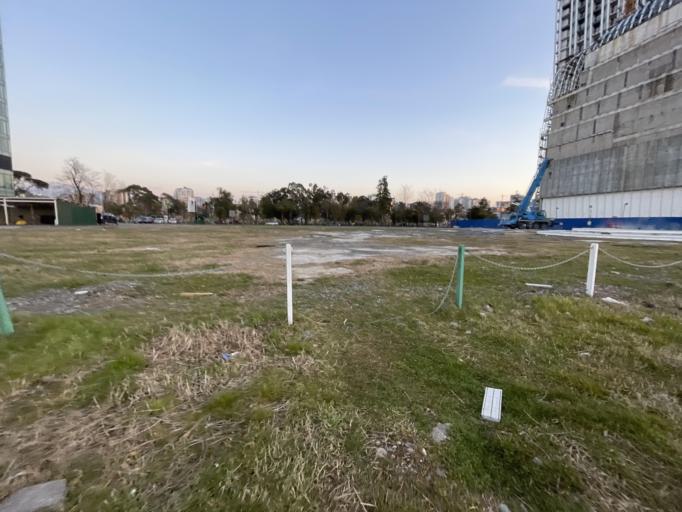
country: GE
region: Ajaria
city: Batumi
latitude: 41.6493
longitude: 41.6244
